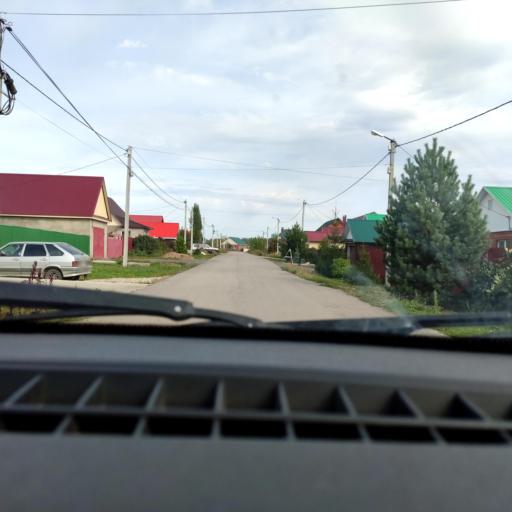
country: RU
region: Bashkortostan
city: Avdon
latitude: 54.6567
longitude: 55.7326
